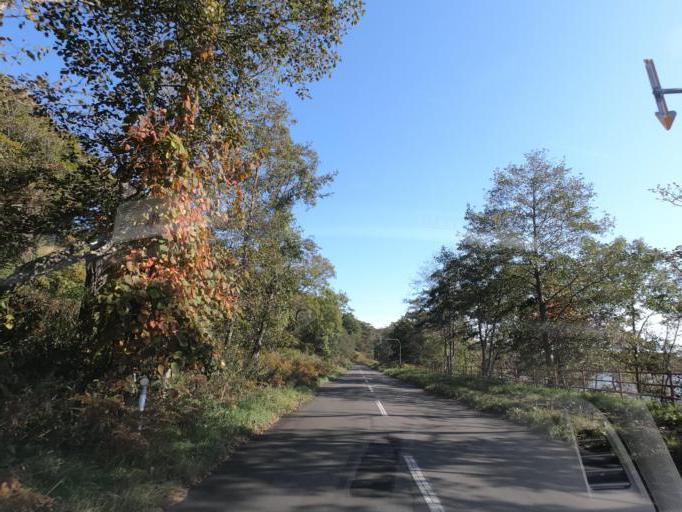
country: JP
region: Hokkaido
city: Obihiro
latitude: 42.6087
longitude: 143.5473
